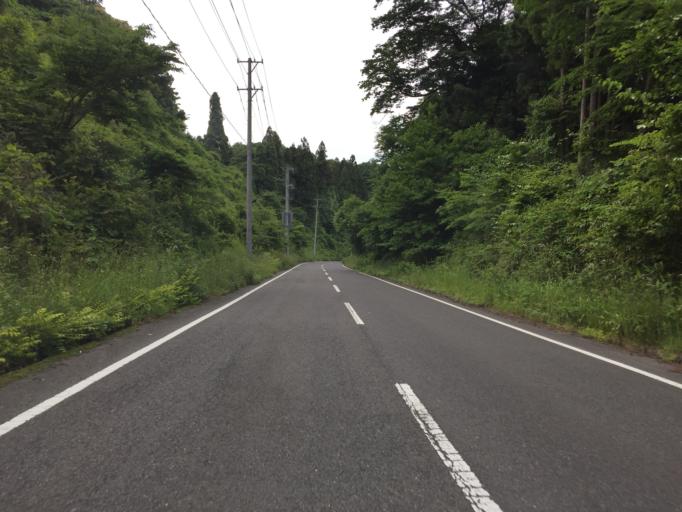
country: JP
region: Fukushima
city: Funehikimachi-funehiki
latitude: 37.4106
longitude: 140.6482
